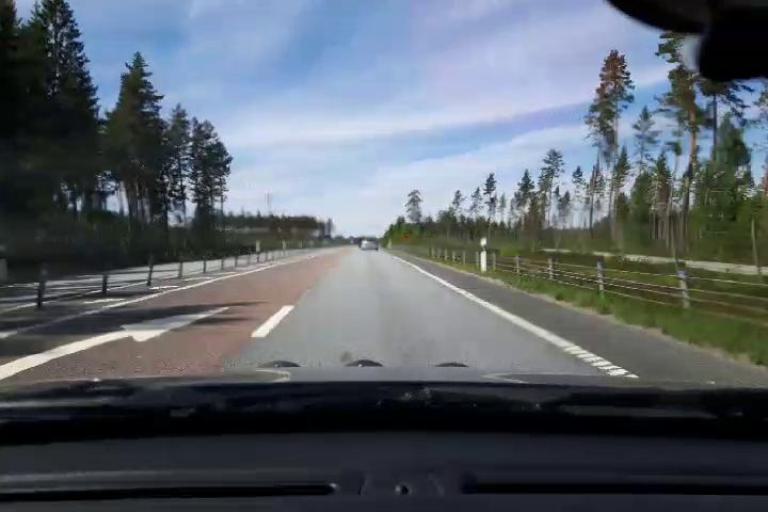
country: SE
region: Gaevleborg
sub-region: Gavle Kommun
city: Norrsundet
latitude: 61.0335
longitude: 16.9718
